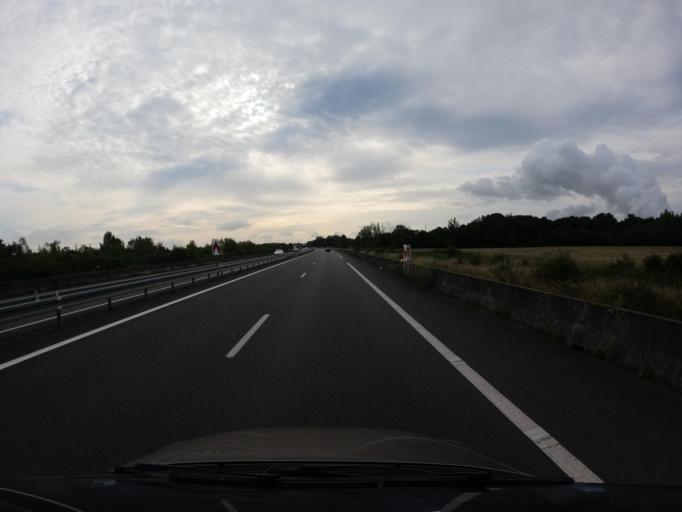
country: FR
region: Centre
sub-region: Departement d'Indre-et-Loire
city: Bourgueil
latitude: 47.2577
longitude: 0.1554
